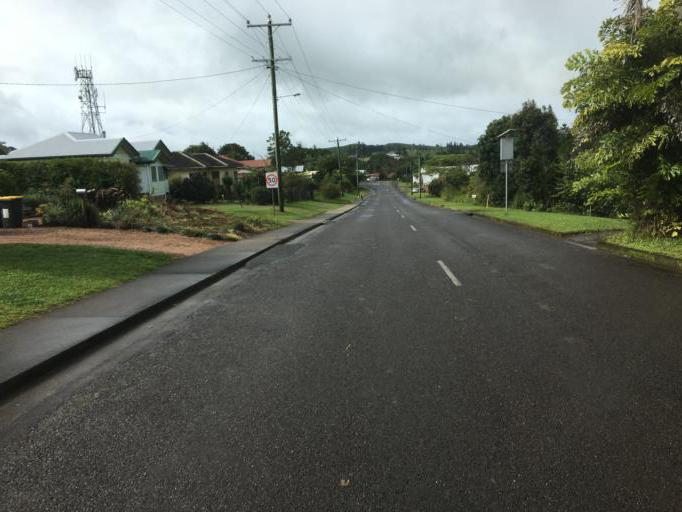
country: AU
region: Queensland
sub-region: Tablelands
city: Ravenshoe
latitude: -17.5130
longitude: 145.6105
